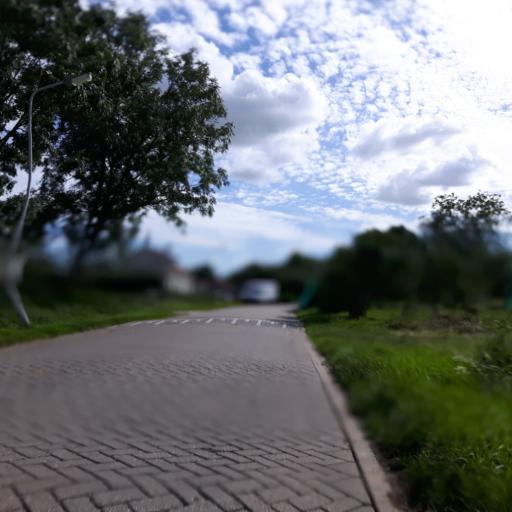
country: NL
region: Zeeland
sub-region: Gemeente Goes
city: Goes
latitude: 51.4990
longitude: 3.9248
